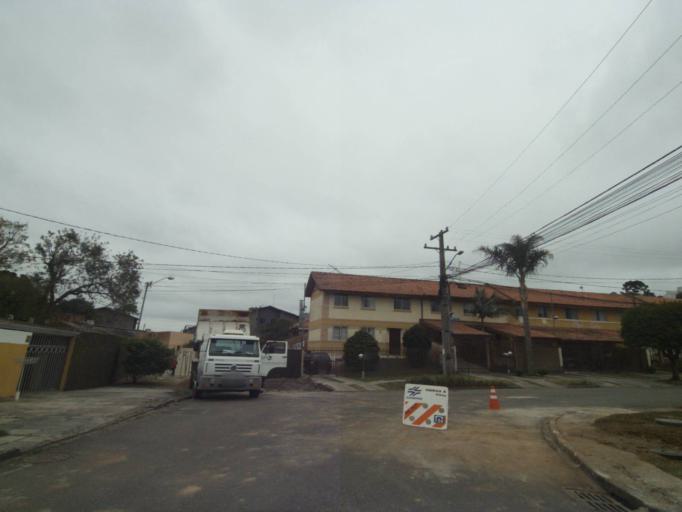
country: BR
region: Parana
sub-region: Pinhais
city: Pinhais
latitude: -25.4768
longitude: -49.2384
